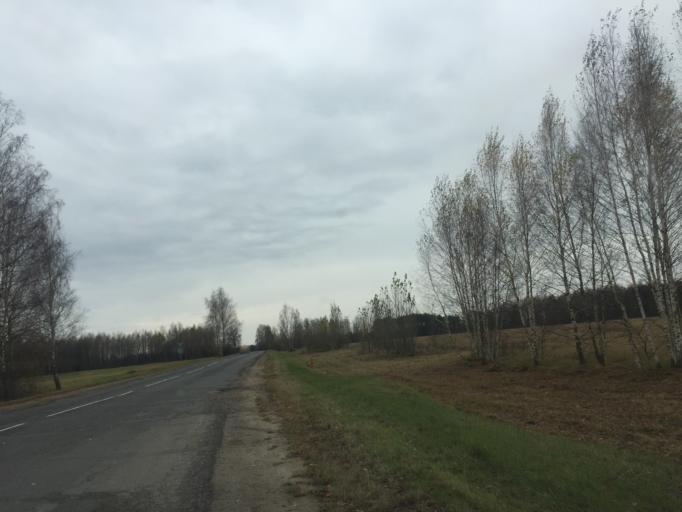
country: BY
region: Mogilev
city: Drybin
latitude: 54.1056
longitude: 31.0939
